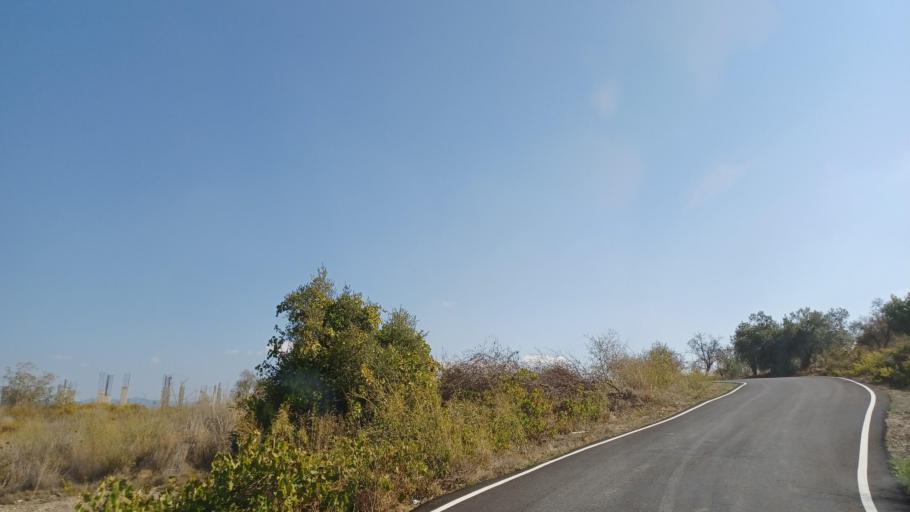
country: CY
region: Pafos
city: Tala
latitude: 34.9121
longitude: 32.4629
